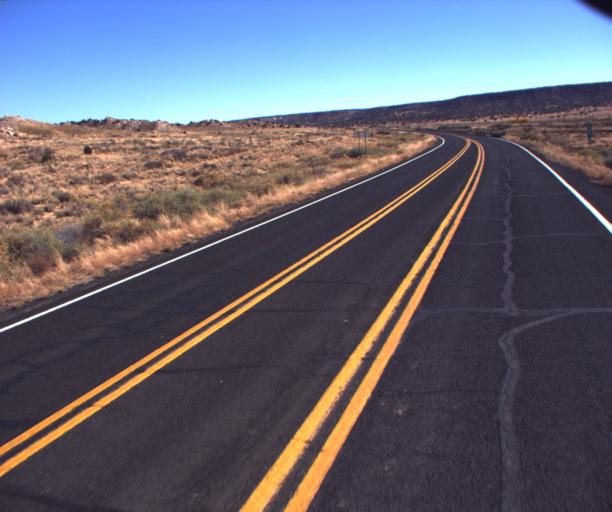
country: US
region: Arizona
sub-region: Navajo County
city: First Mesa
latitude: 35.8315
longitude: -110.2928
